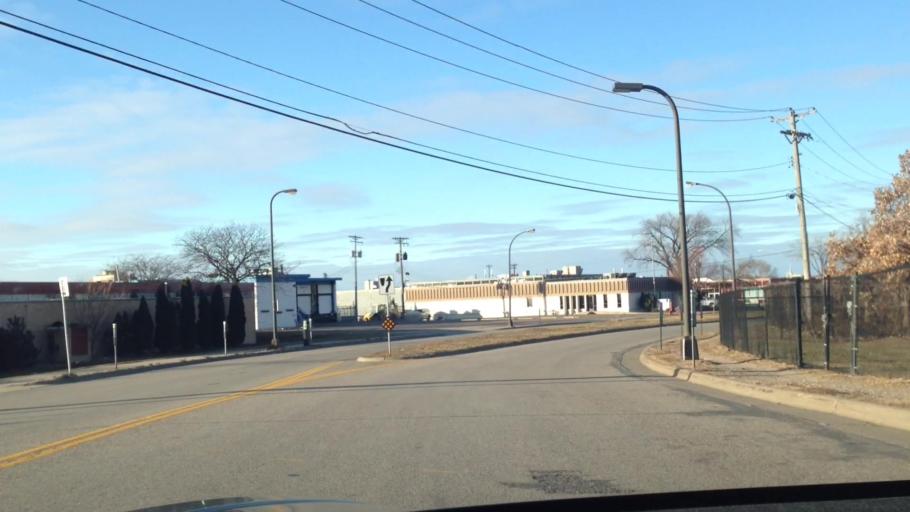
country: US
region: Minnesota
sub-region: Hennepin County
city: Minneapolis
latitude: 44.9802
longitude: -93.2826
